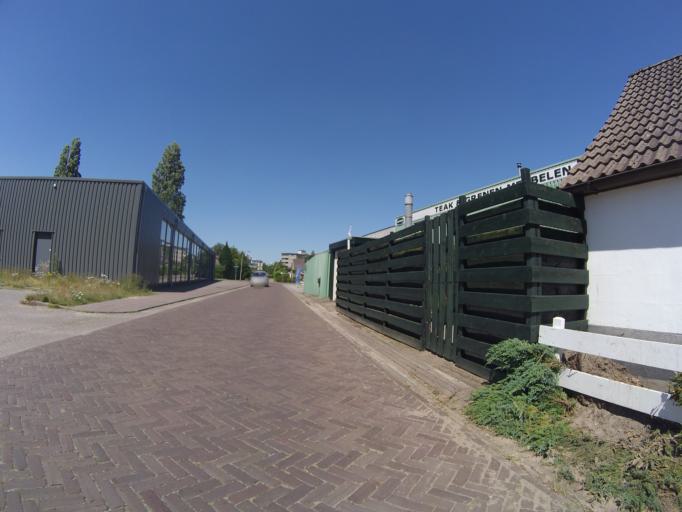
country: NL
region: Drenthe
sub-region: Gemeente Emmen
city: Emmen
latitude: 52.7773
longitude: 6.8996
